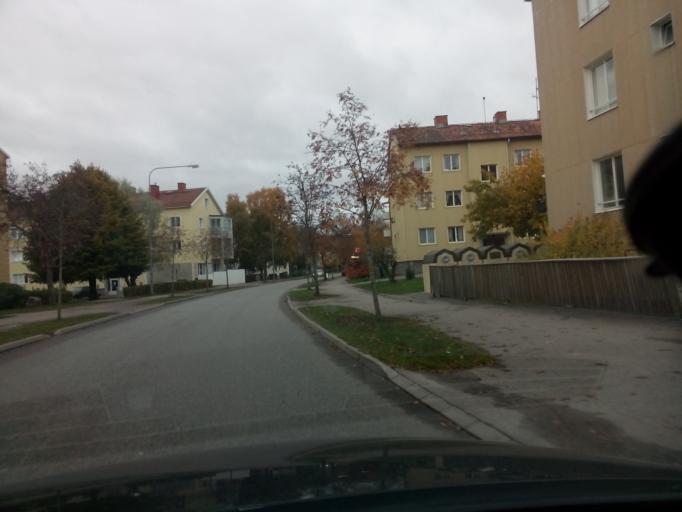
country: SE
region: Soedermanland
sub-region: Nykopings Kommun
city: Nykoping
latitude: 58.7516
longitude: 17.0252
